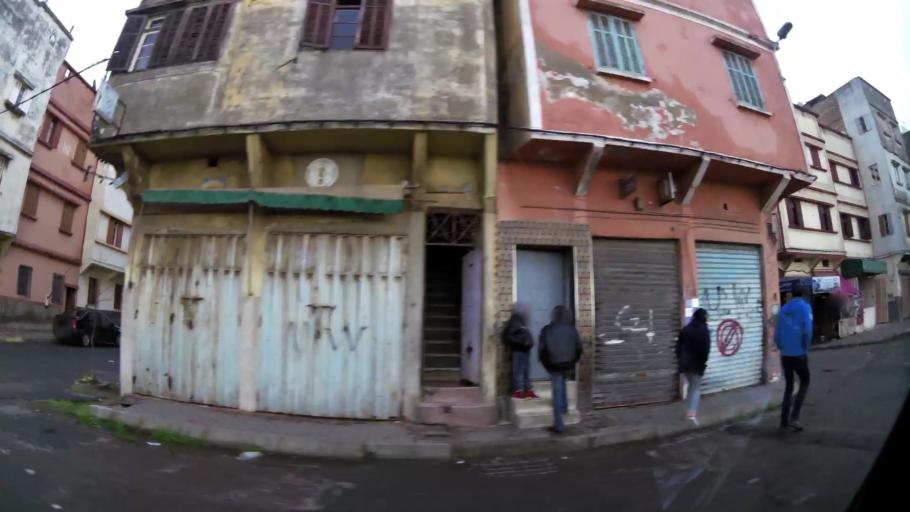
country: MA
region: Grand Casablanca
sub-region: Casablanca
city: Casablanca
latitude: 33.5551
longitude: -7.5771
